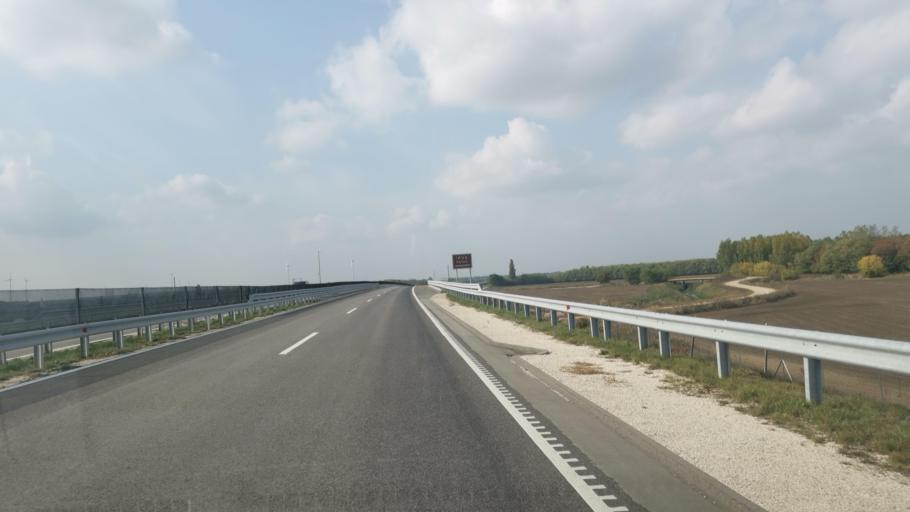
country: HU
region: Gyor-Moson-Sopron
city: Fertoszentmiklos
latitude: 47.5711
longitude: 16.7977
